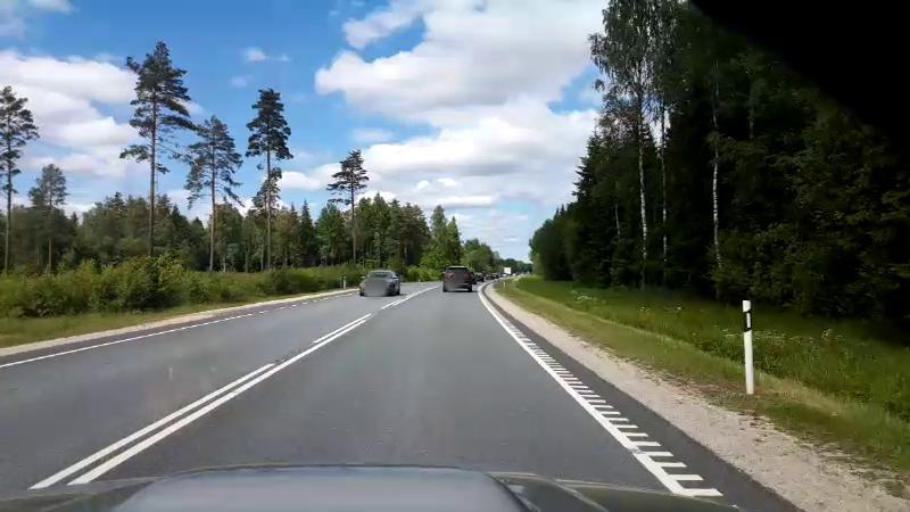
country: EE
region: Raplamaa
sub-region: Maerjamaa vald
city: Marjamaa
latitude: 59.0329
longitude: 24.4442
